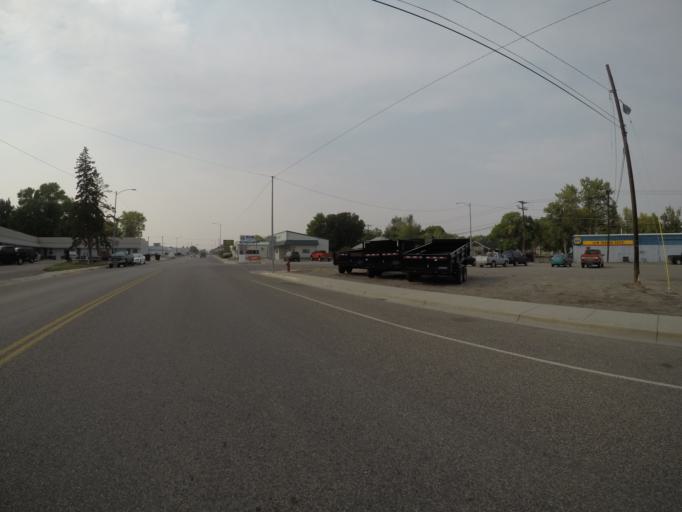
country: US
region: Montana
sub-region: Yellowstone County
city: Laurel
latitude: 45.6683
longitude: -108.7756
